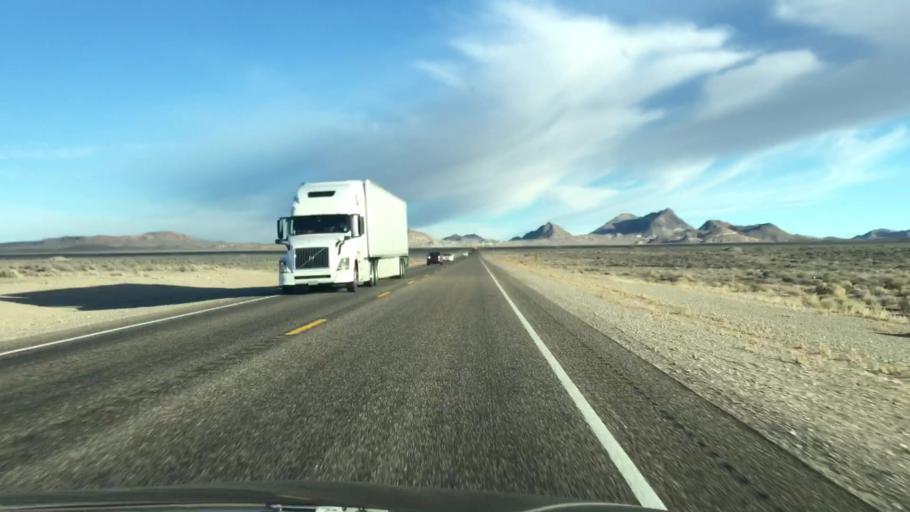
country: US
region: Nevada
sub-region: Nye County
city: Tonopah
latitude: 38.0987
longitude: -117.3242
